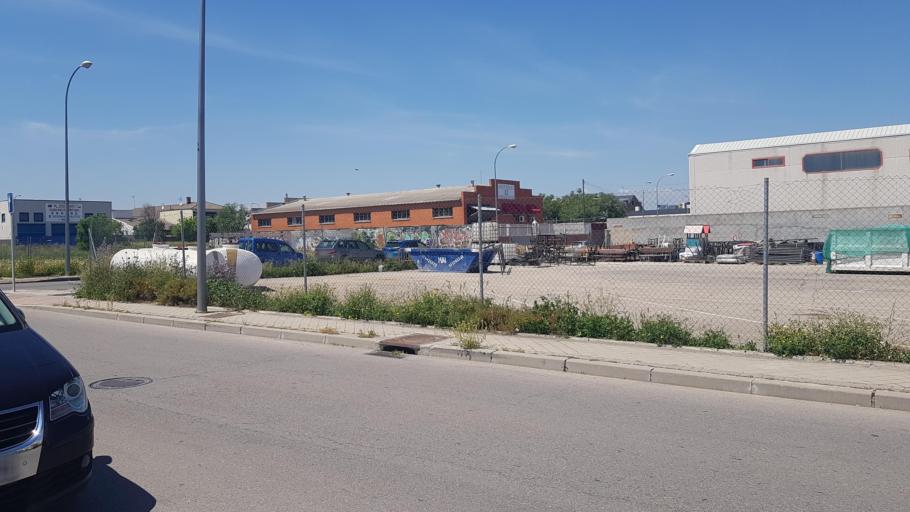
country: ES
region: Madrid
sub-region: Provincia de Madrid
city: Coslada
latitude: 40.4418
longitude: -3.5660
